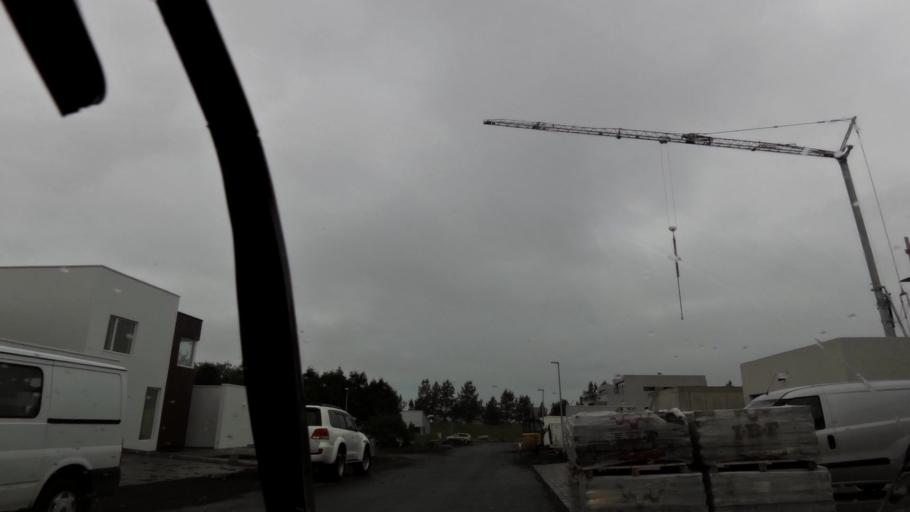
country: IS
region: Capital Region
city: Reykjavik
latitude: 64.1206
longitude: -21.8951
